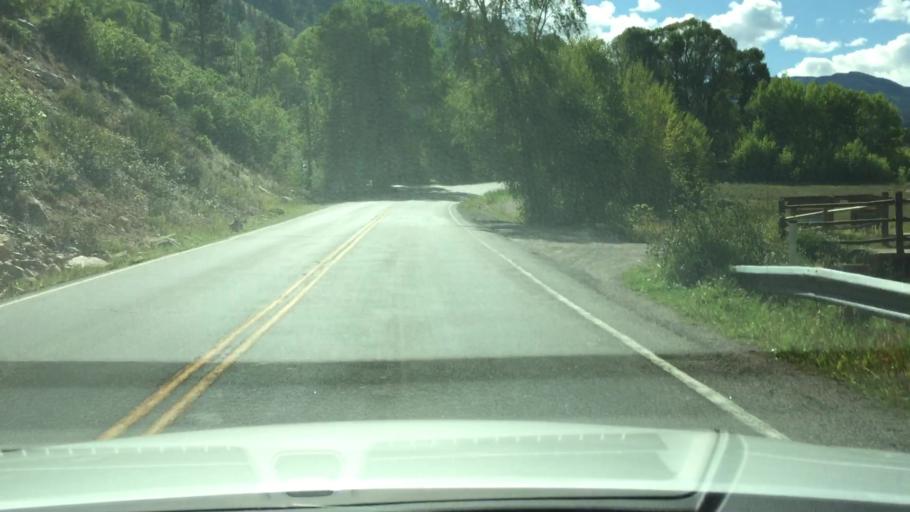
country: US
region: Colorado
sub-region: Pitkin County
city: Aspen
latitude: 39.1770
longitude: -106.7961
